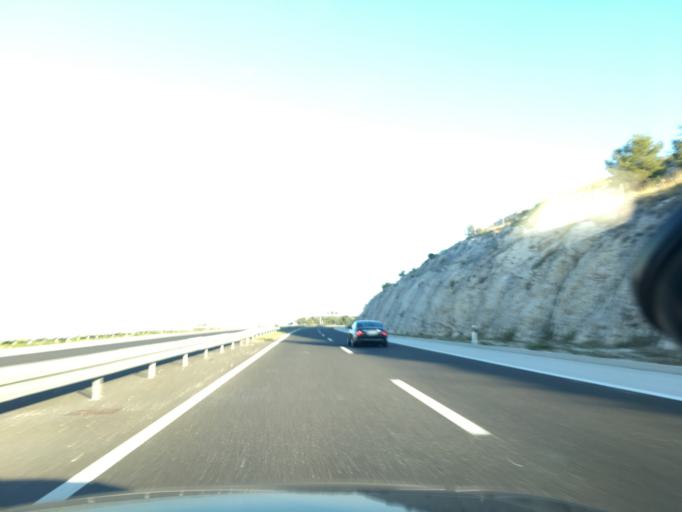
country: HR
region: Sibensko-Kniniska
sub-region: Grad Sibenik
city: Brodarica
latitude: 43.7238
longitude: 15.9823
